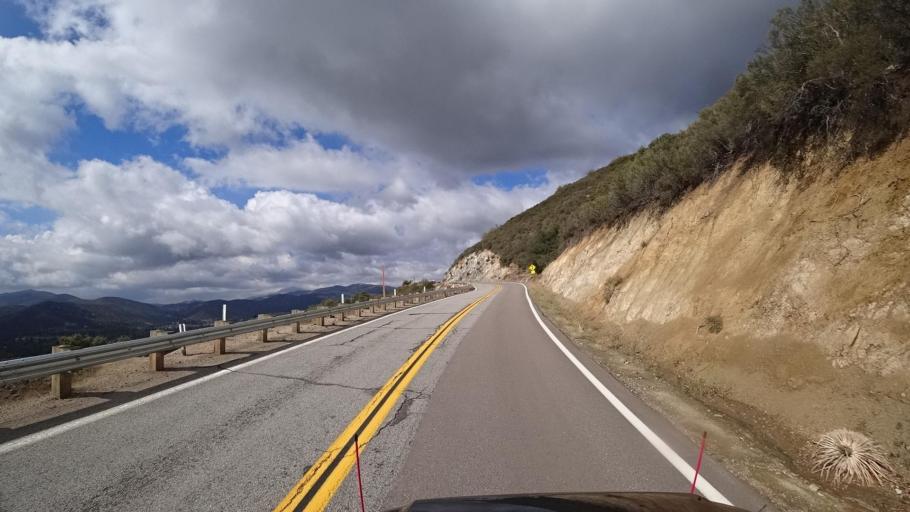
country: US
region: California
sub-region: San Diego County
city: Pine Valley
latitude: 32.8168
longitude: -116.5098
